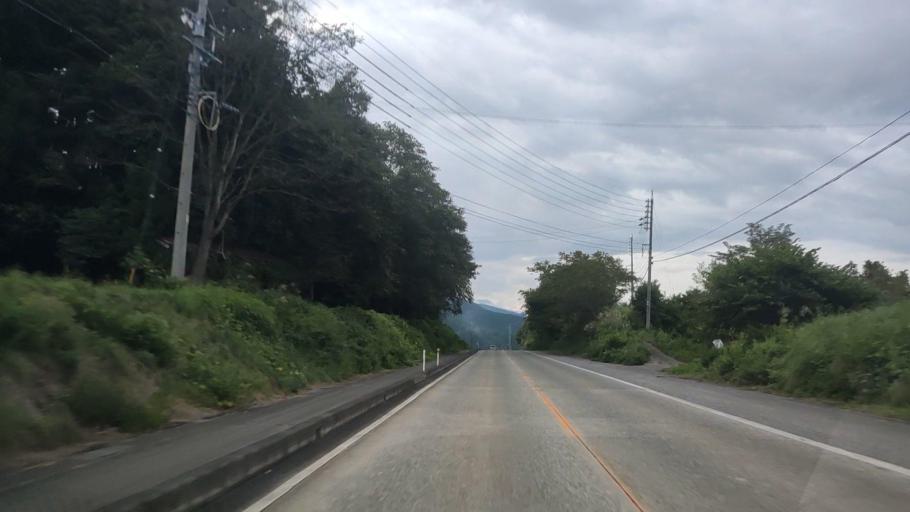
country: JP
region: Nagano
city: Iiyama
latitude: 36.8887
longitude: 138.4088
